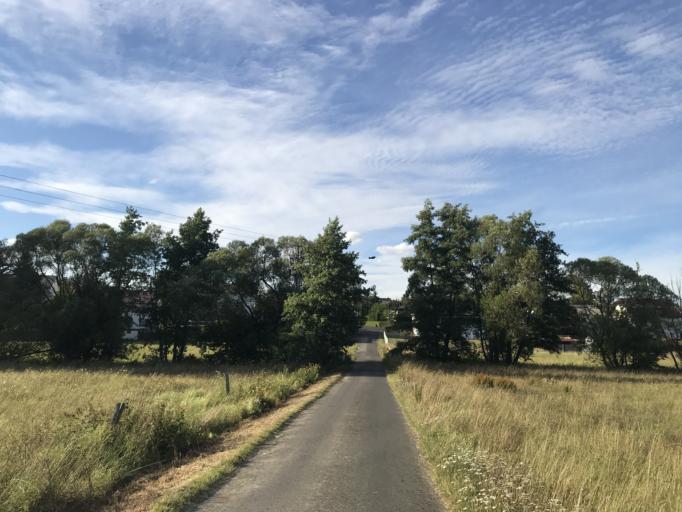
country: DE
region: Hesse
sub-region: Regierungsbezirk Giessen
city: Lohra
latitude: 50.6861
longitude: 8.6020
